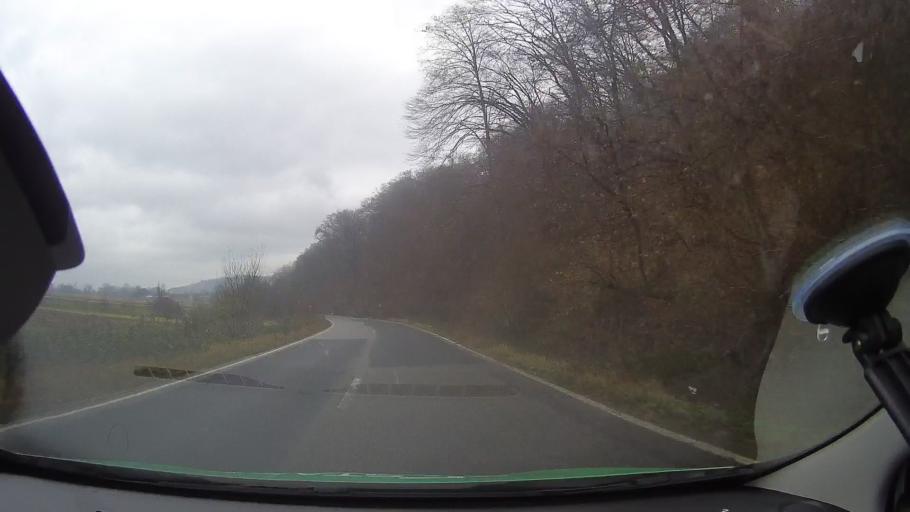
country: RO
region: Arad
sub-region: Comuna Buteni
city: Buteni
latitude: 46.3003
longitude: 22.1645
